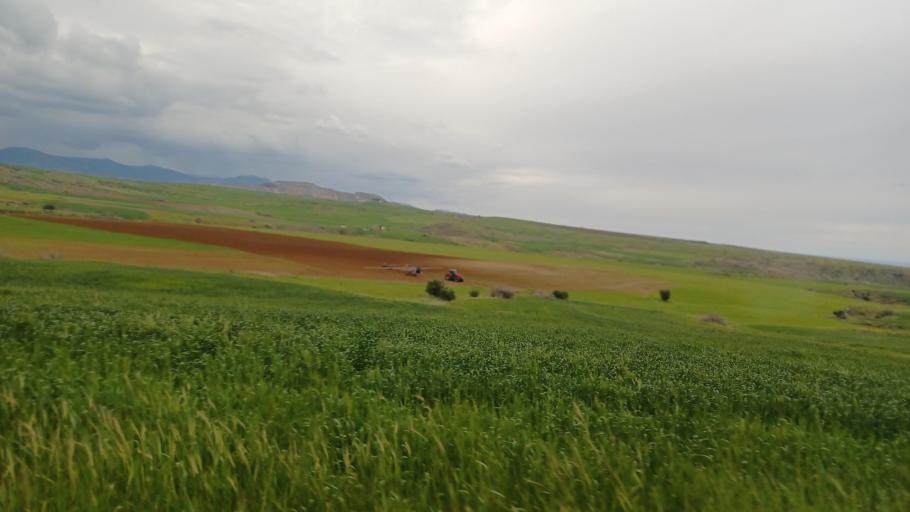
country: CY
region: Lefkosia
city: Astromeritis
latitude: 35.0929
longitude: 32.9514
